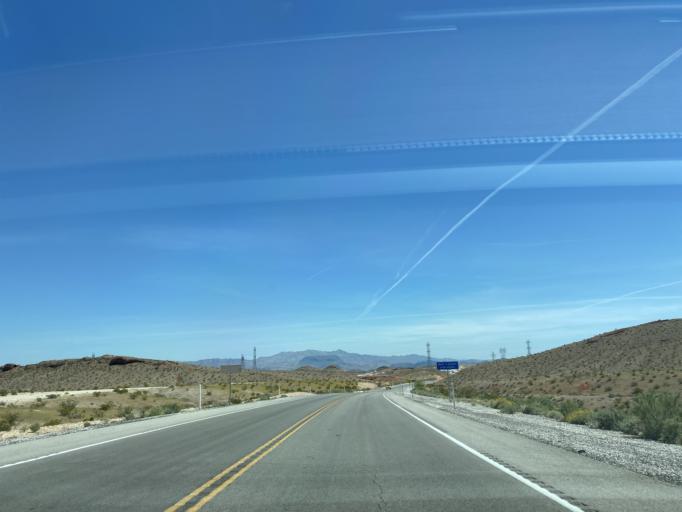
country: US
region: Nevada
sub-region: Clark County
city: Nellis Air Force Base
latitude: 36.1942
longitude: -114.9239
